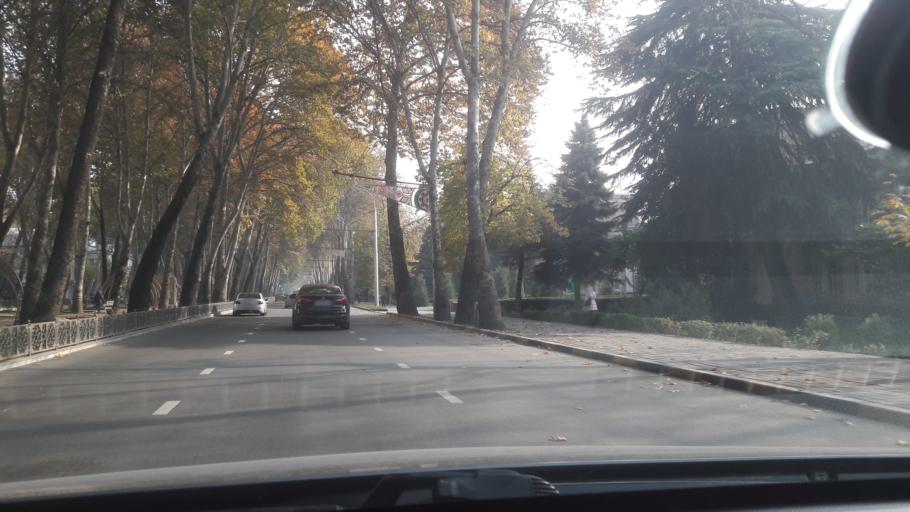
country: TJ
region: Dushanbe
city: Dushanbe
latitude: 38.5697
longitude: 68.7910
